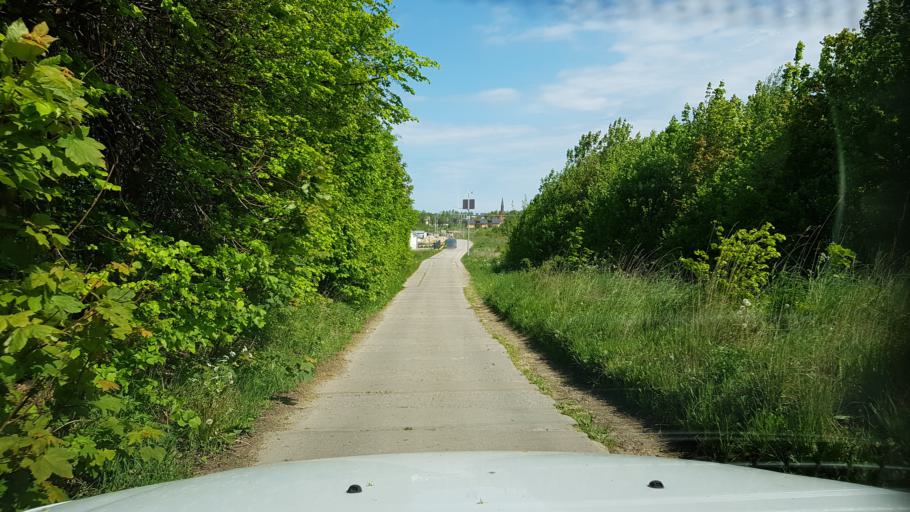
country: PL
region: West Pomeranian Voivodeship
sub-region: Powiat koszalinski
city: Mielno
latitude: 54.2377
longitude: 15.9554
